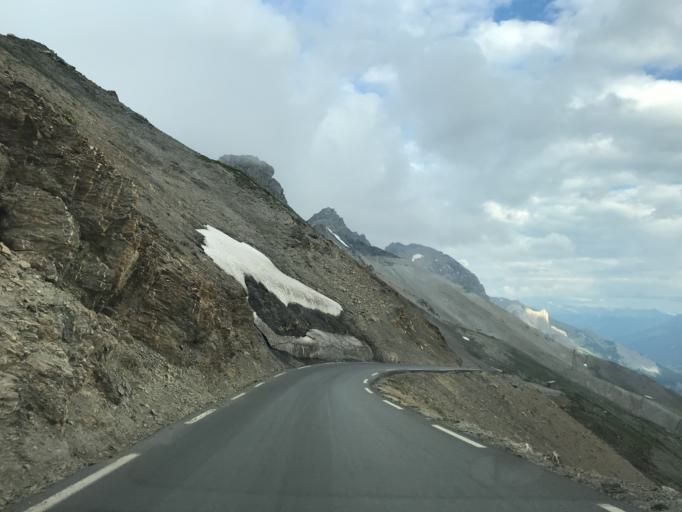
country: FR
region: Rhone-Alpes
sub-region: Departement de la Savoie
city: Valloire
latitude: 45.0639
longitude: 6.4084
